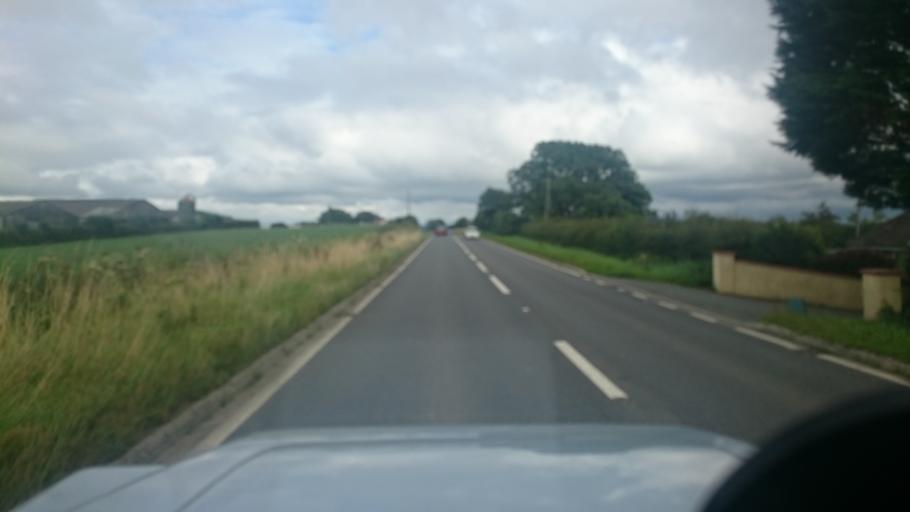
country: GB
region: Wales
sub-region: Pembrokeshire
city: Wiston
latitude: 51.8000
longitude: -4.8427
